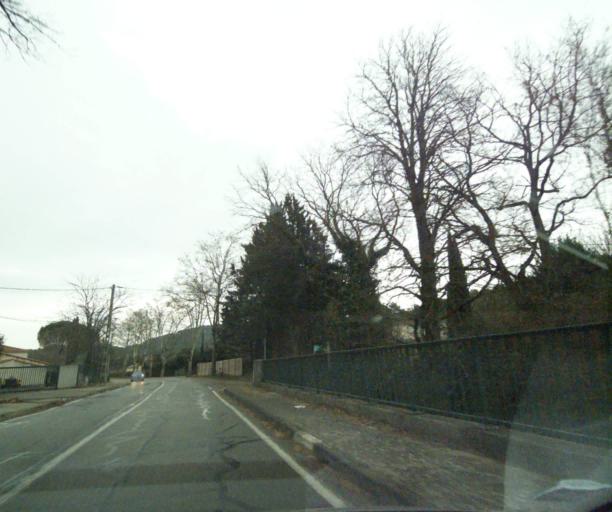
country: FR
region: Provence-Alpes-Cote d'Azur
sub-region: Departement des Bouches-du-Rhone
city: Le Puy-Sainte-Reparade
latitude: 43.6589
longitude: 5.4136
